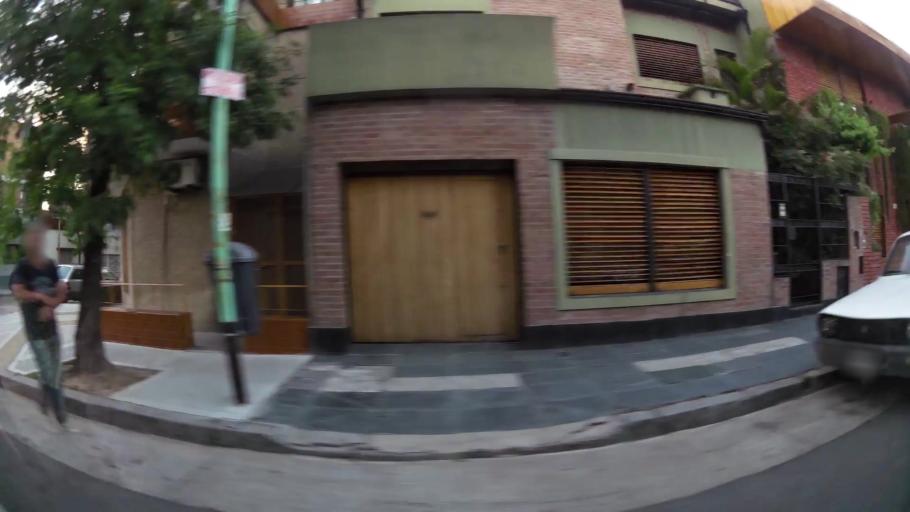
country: AR
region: Buenos Aires
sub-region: Partido de Vicente Lopez
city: Olivos
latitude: -34.5424
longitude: -58.4800
